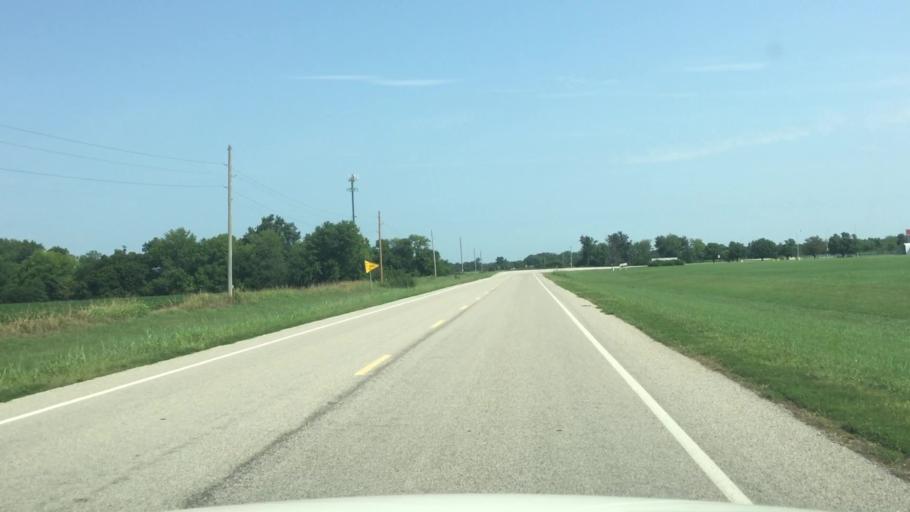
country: US
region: Kansas
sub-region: Montgomery County
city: Coffeyville
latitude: 37.1013
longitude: -95.5861
